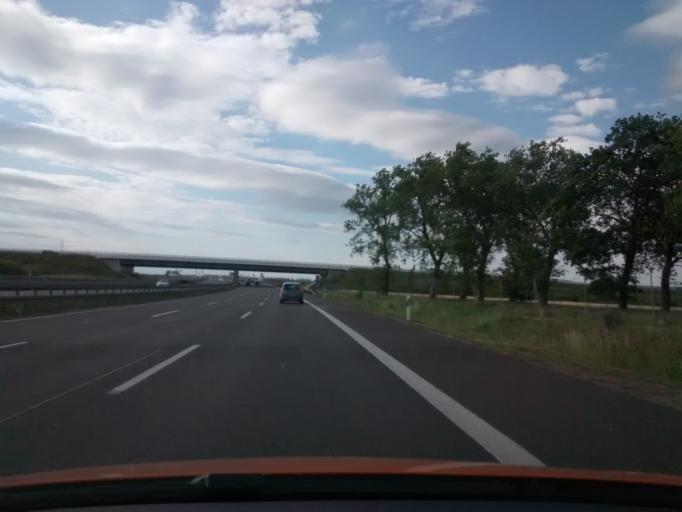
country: DE
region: Brandenburg
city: Schonefeld
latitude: 52.3715
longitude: 13.5477
